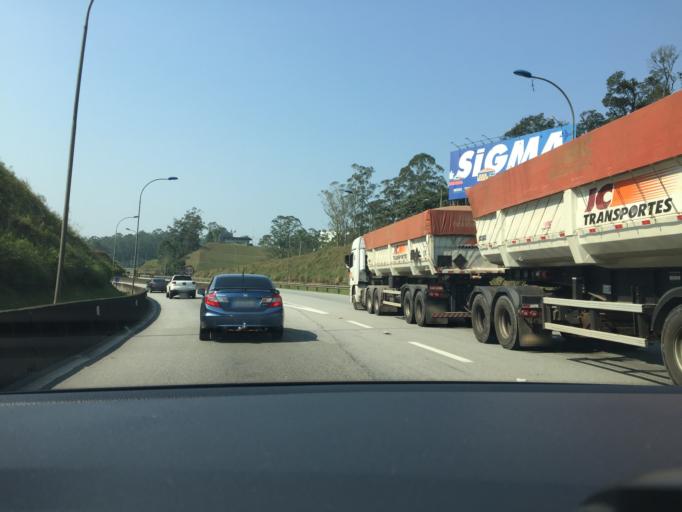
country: BR
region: Sao Paulo
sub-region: Sao Bernardo Do Campo
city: Sao Bernardo do Campo
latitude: -23.7682
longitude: -46.5901
